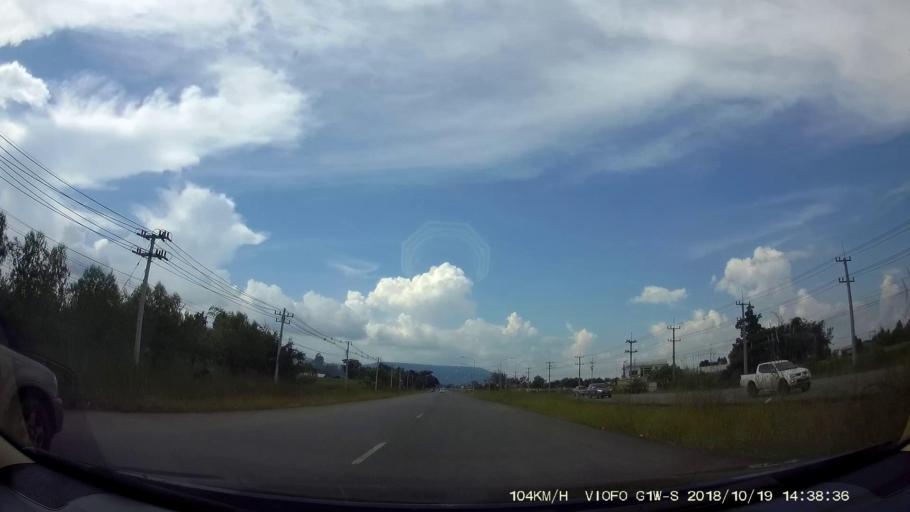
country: TH
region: Chaiyaphum
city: Kaeng Khro
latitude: 16.2154
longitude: 102.2006
